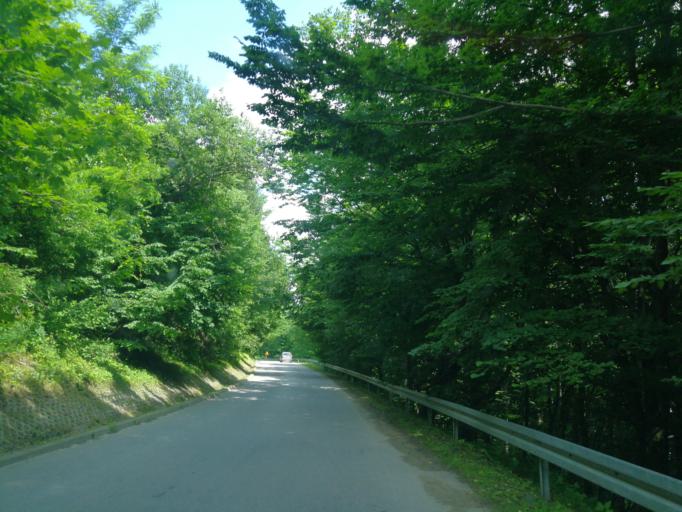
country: PL
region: Subcarpathian Voivodeship
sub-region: Powiat leski
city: Polanczyk
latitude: 49.4178
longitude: 22.4327
